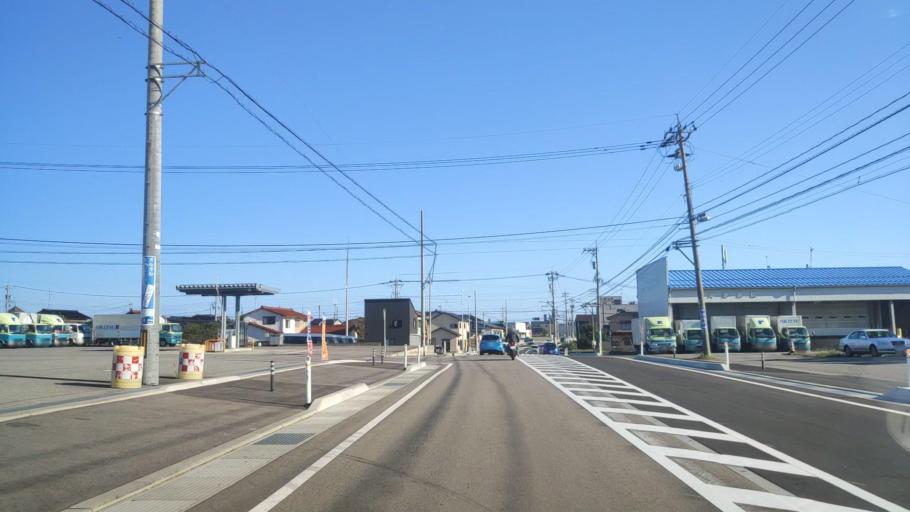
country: JP
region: Ishikawa
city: Tsubata
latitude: 36.7291
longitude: 136.6988
